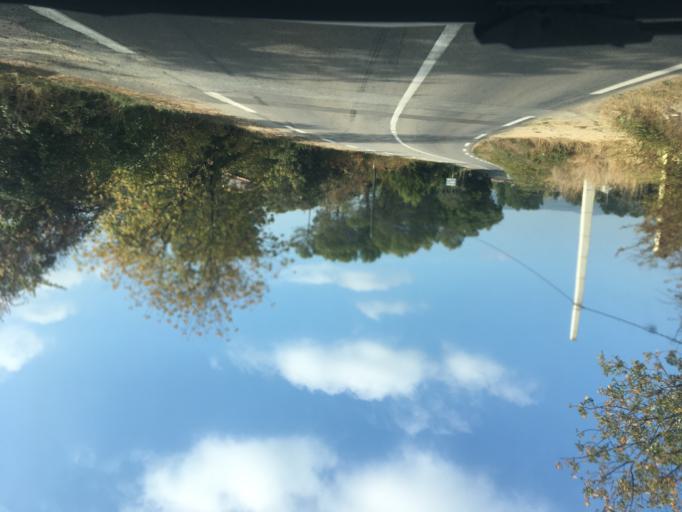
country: FR
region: Provence-Alpes-Cote d'Azur
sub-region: Departement du Var
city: Flayosc
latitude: 43.5079
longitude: 6.4239
